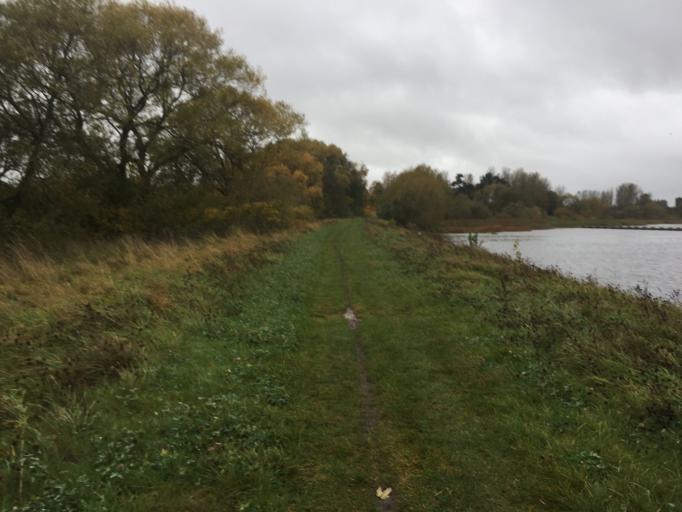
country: DK
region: Zealand
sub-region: Ringsted Kommune
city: Ringsted
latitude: 55.4820
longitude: 11.7524
